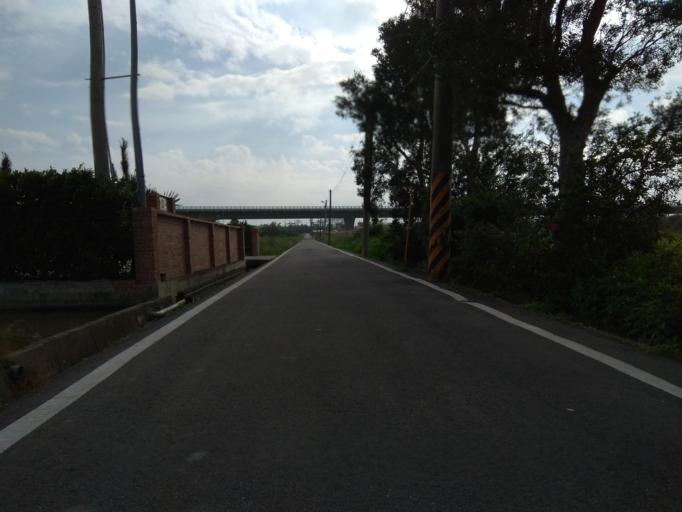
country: TW
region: Taiwan
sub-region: Hsinchu
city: Zhubei
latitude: 24.9650
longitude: 121.0110
